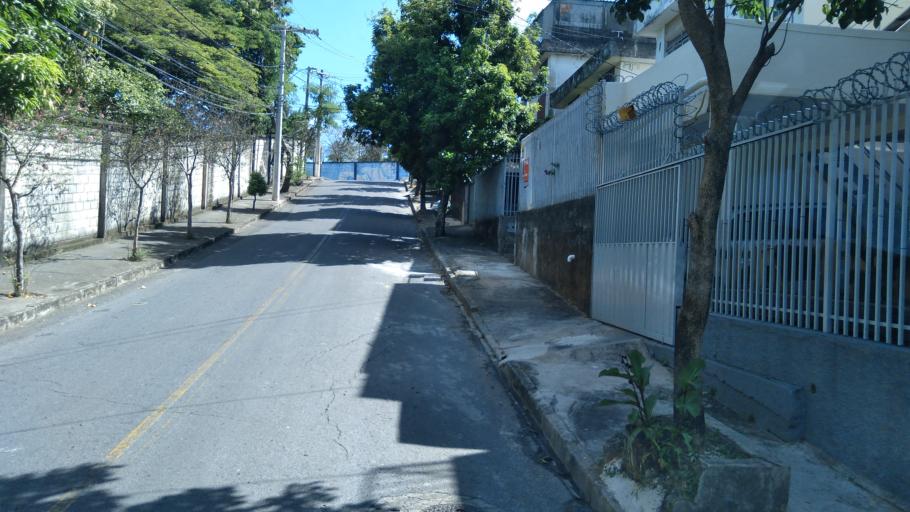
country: BR
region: Minas Gerais
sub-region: Belo Horizonte
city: Belo Horizonte
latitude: -19.8512
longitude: -43.9137
